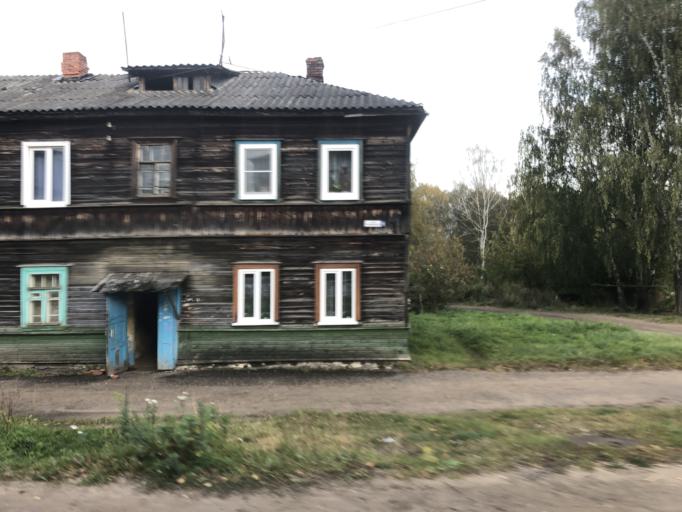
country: RU
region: Tverskaya
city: Rzhev
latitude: 56.2539
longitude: 34.2930
